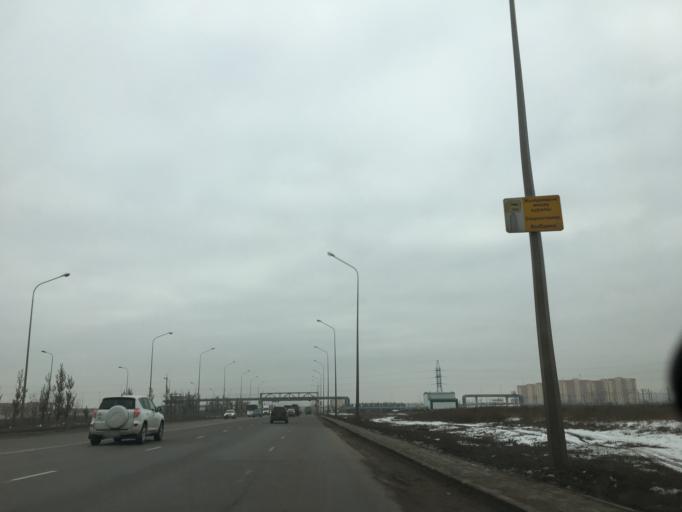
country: KZ
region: Astana Qalasy
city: Astana
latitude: 51.1626
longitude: 71.5125
